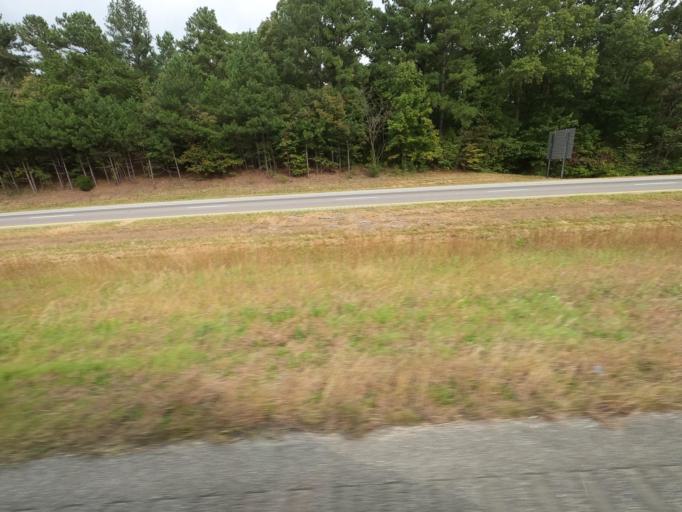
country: US
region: Tennessee
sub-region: Dickson County
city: Dickson
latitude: 35.9971
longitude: -87.4651
